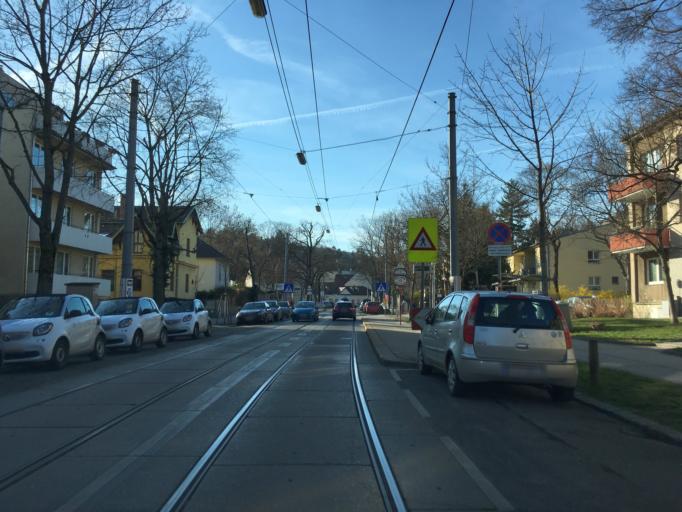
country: AT
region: Vienna
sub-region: Wien Stadt
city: Vienna
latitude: 48.2304
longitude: 16.2969
